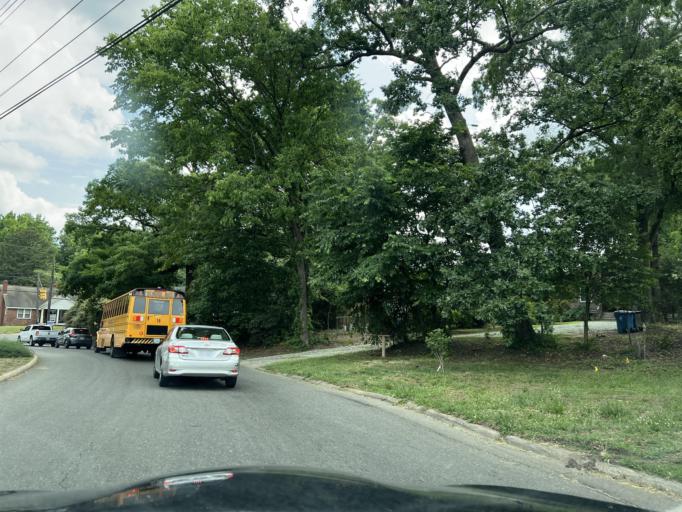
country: US
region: North Carolina
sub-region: Durham County
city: Durham
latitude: 36.0043
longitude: -78.8861
